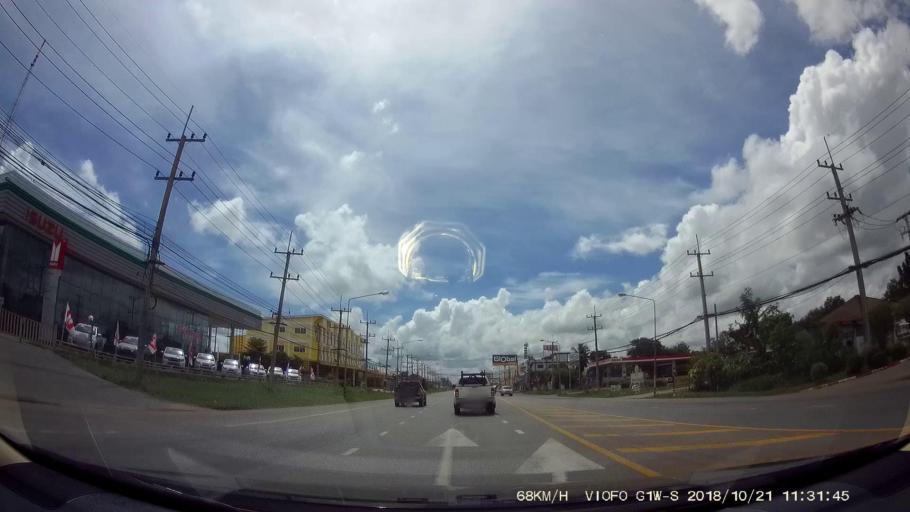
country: TH
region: Chaiyaphum
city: Chaiyaphum
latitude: 15.7663
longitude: 102.0252
